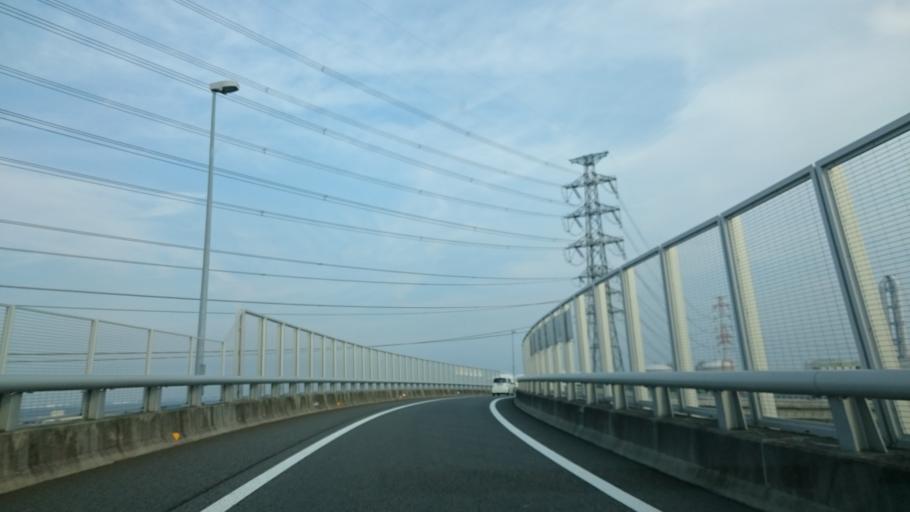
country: JP
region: Mie
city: Yokkaichi
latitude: 35.0213
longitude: 136.6858
